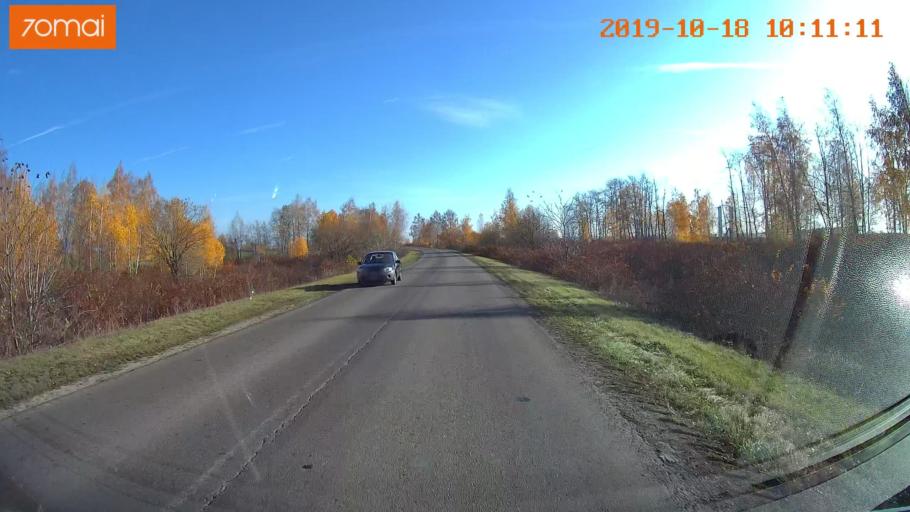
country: RU
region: Tula
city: Kurkino
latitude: 53.3809
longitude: 38.4928
